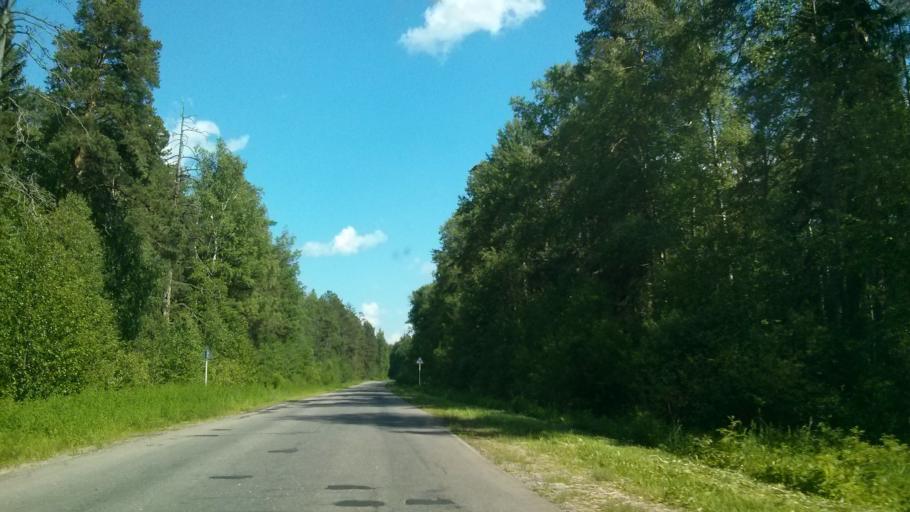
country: RU
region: Vladimir
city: Melenki
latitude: 55.3332
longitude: 41.6798
